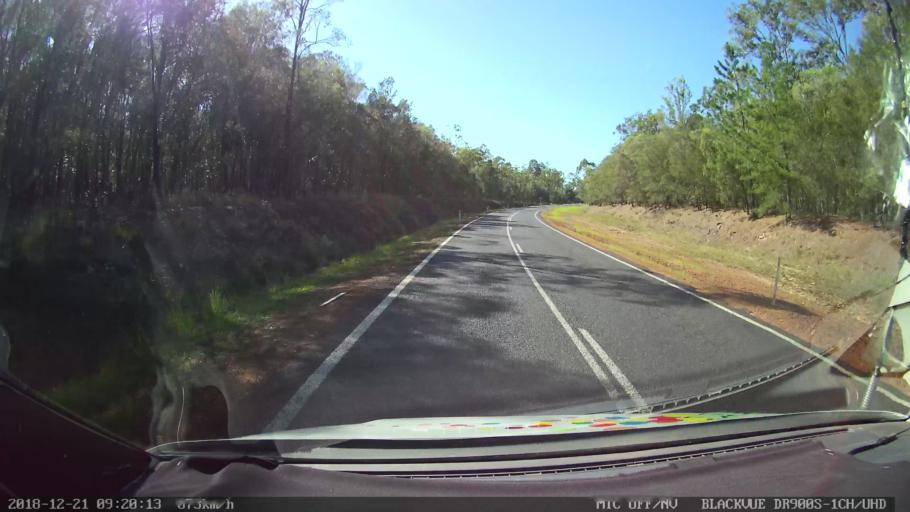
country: AU
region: New South Wales
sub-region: Clarence Valley
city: Maclean
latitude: -29.3123
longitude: 152.9997
